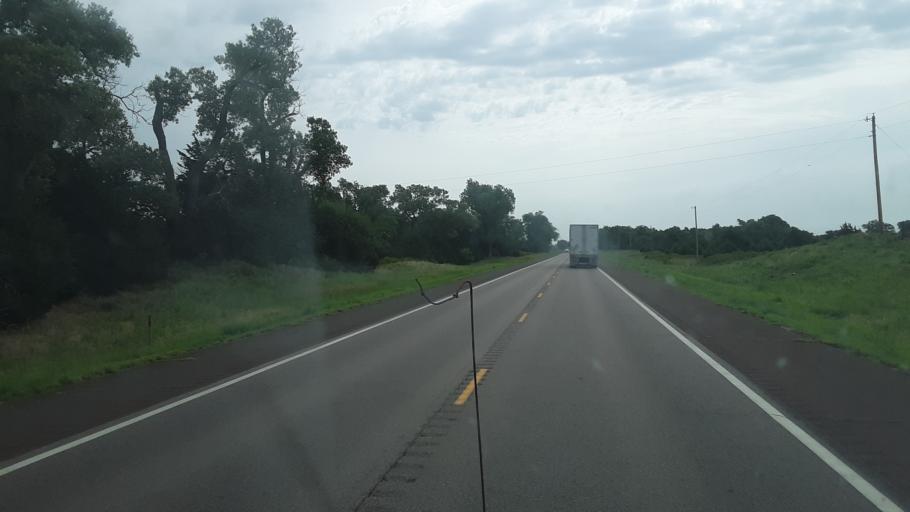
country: US
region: Kansas
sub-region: Stafford County
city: Saint John
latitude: 37.9557
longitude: -98.7178
